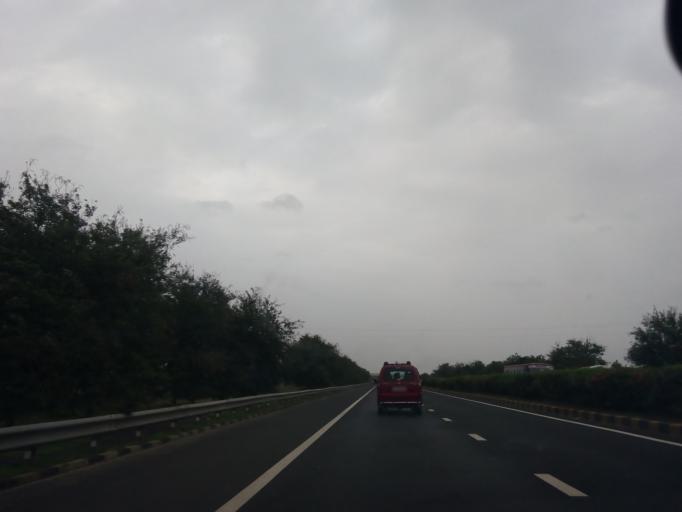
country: IN
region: Gujarat
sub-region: Kheda
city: Mahemdavad
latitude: 22.8290
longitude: 72.8259
